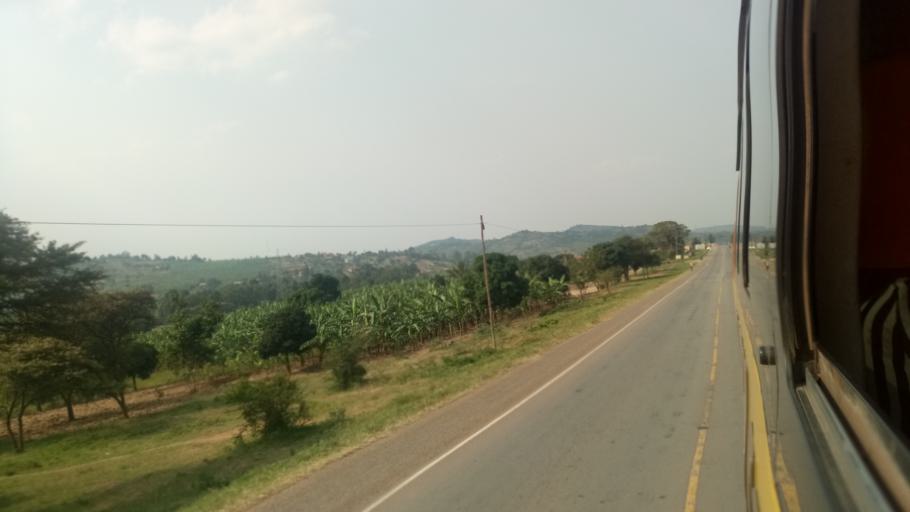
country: UG
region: Western Region
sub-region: Mbarara District
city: Mbarara
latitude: -0.5276
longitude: 30.7258
